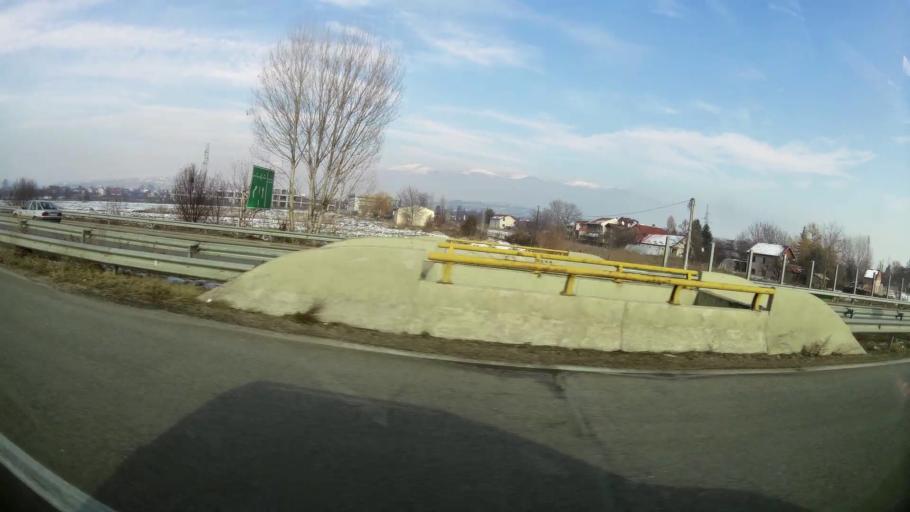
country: MK
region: Butel
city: Butel
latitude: 42.0427
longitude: 21.4477
